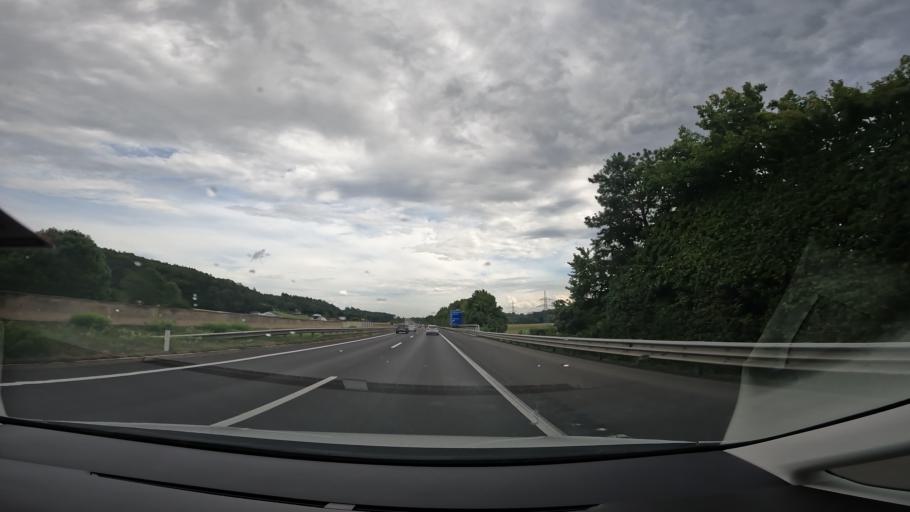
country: AT
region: Styria
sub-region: Politischer Bezirk Leibnitz
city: Lang
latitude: 46.8621
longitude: 15.4984
